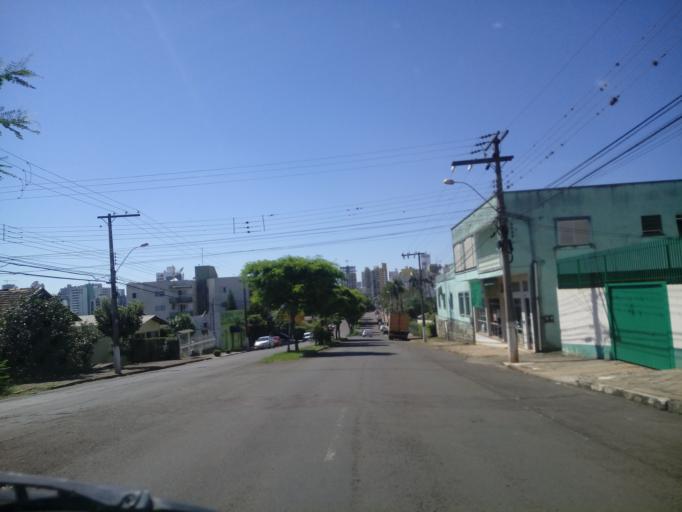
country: BR
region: Santa Catarina
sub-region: Chapeco
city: Chapeco
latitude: -27.1037
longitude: -52.6237
